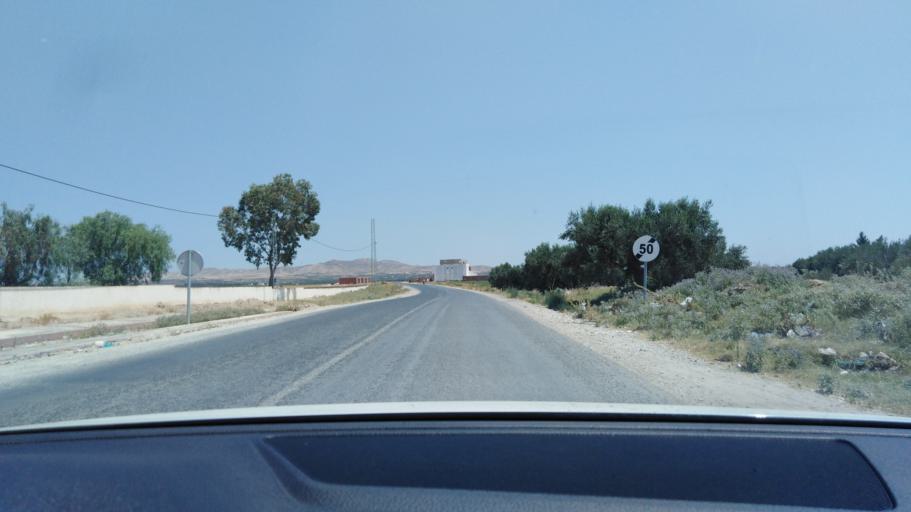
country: TN
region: Al Qayrawan
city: Sbikha
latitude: 36.1142
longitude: 10.0989
